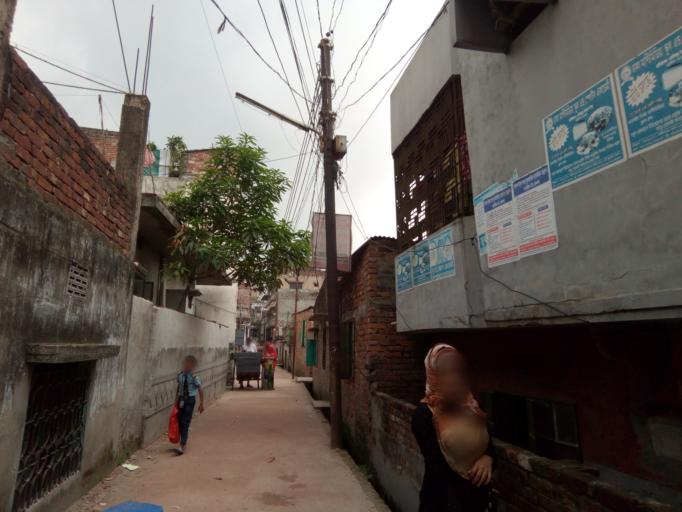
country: BD
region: Dhaka
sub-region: Dhaka
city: Dhaka
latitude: 23.6915
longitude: 90.4471
